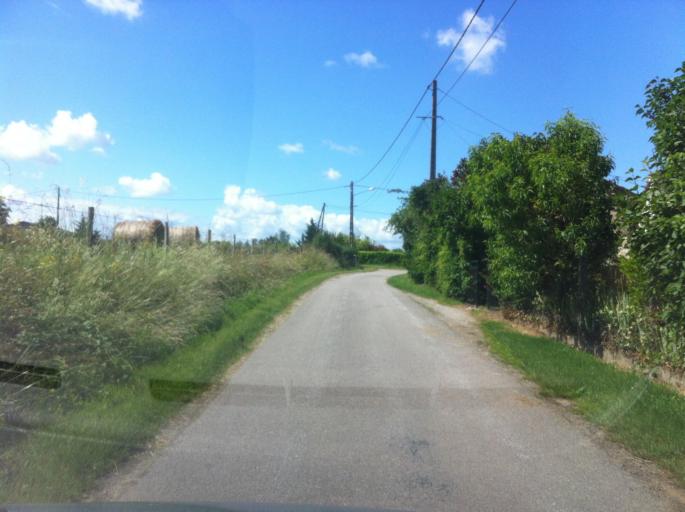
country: FR
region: Auvergne
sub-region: Departement de l'Allier
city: Saint-Pourcain-sur-Sioule
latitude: 46.3037
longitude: 3.2108
